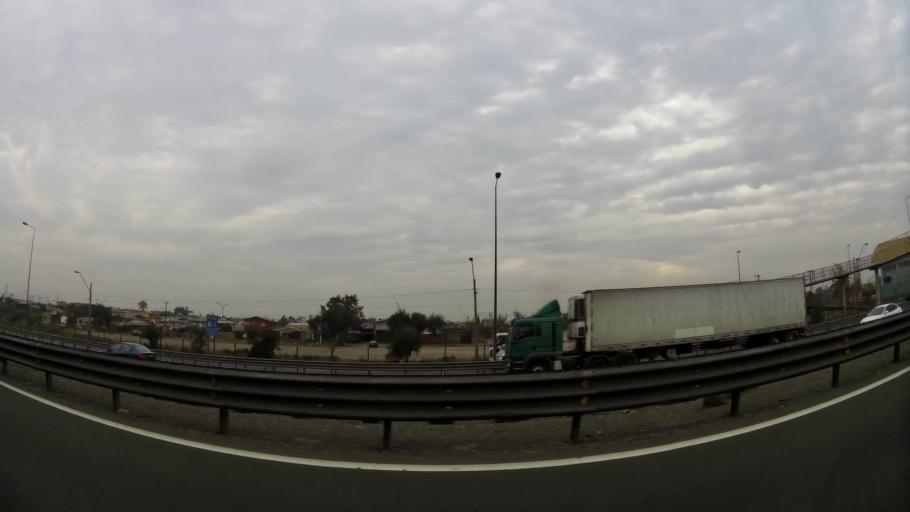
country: CL
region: Santiago Metropolitan
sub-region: Provincia de Santiago
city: Lo Prado
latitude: -33.5053
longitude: -70.7301
